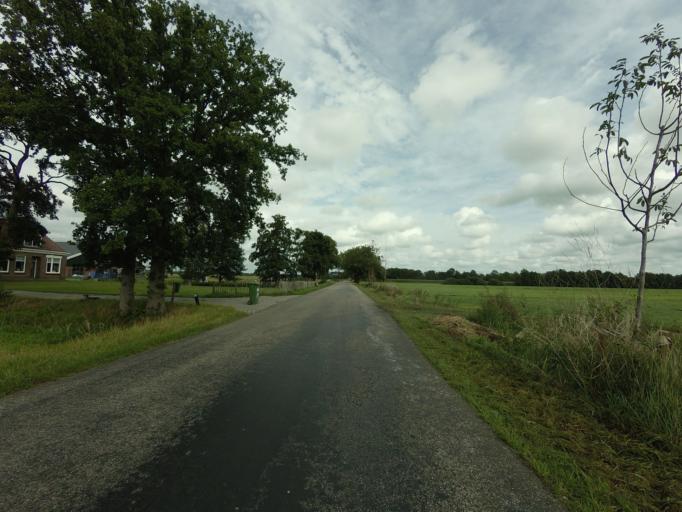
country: NL
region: Friesland
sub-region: Gemeente Heerenveen
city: Nieuwehorne
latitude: 52.9242
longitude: 6.0902
